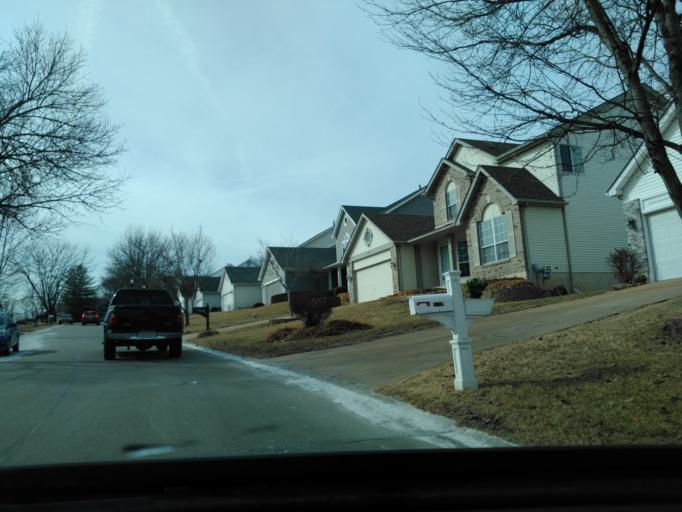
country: US
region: Missouri
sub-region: Saint Louis County
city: Valley Park
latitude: 38.5505
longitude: -90.5137
